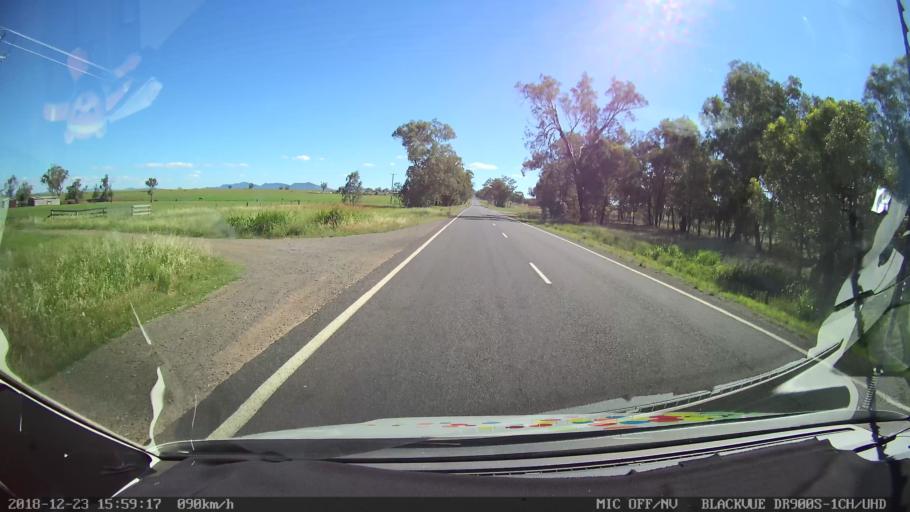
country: AU
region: New South Wales
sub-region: Tamworth Municipality
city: Phillip
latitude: -31.1979
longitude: 150.8345
